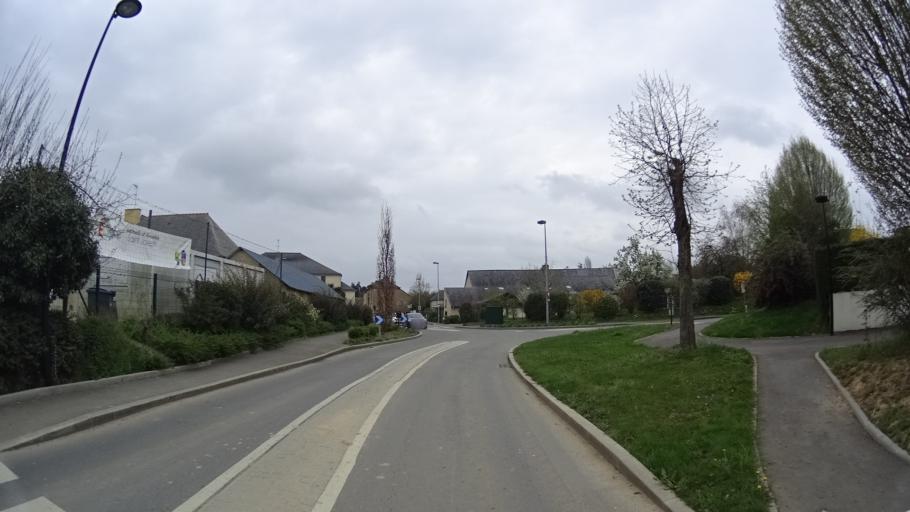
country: FR
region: Brittany
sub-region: Departement d'Ille-et-Vilaine
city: Cintre
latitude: 48.1074
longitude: -1.8722
